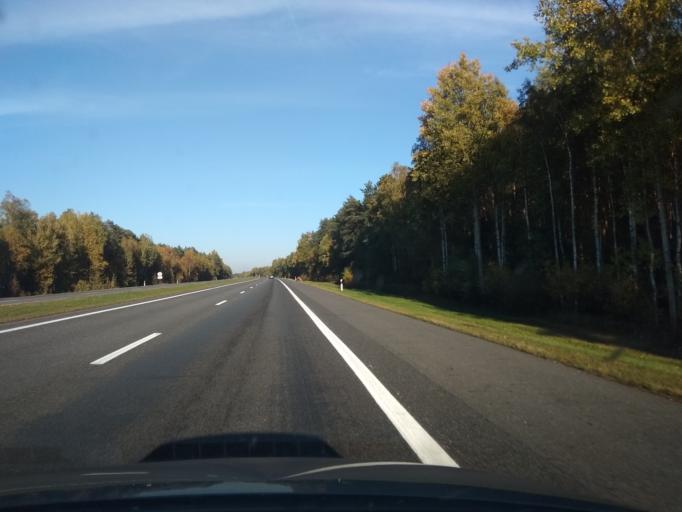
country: BY
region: Brest
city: Nyakhachava
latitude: 52.5806
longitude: 25.1240
